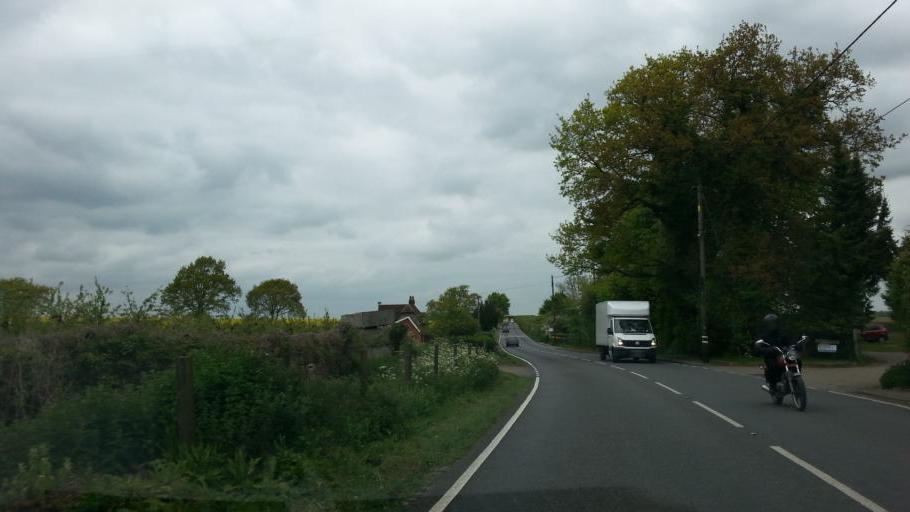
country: GB
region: England
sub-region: Suffolk
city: Thurston
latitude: 52.1870
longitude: 0.7649
